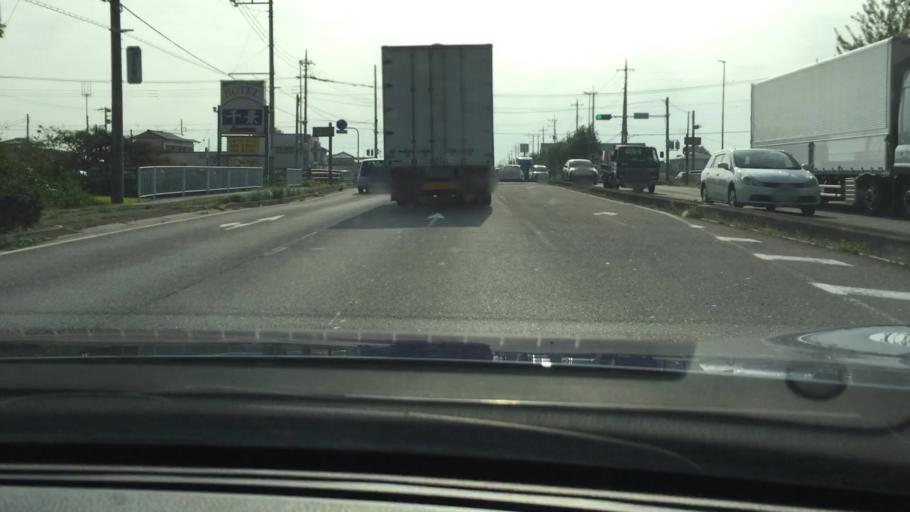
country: JP
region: Saitama
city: Menuma
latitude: 36.2471
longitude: 139.4537
